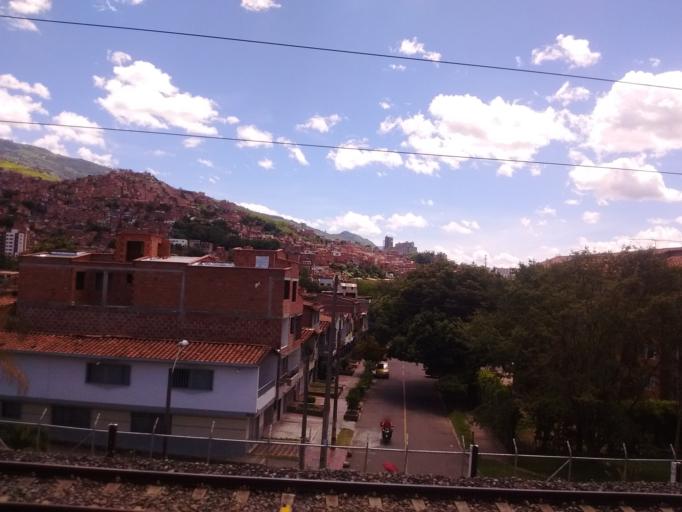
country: CO
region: Antioquia
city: Medellin
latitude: 6.2562
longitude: -75.6125
